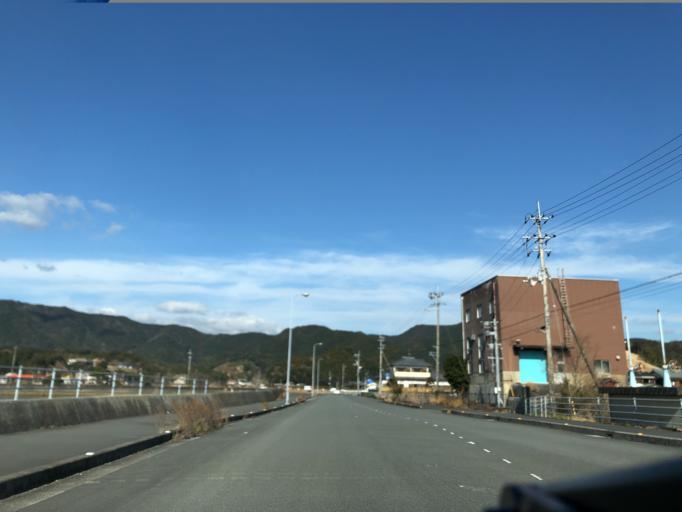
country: JP
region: Kochi
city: Sukumo
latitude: 32.9270
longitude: 132.6969
